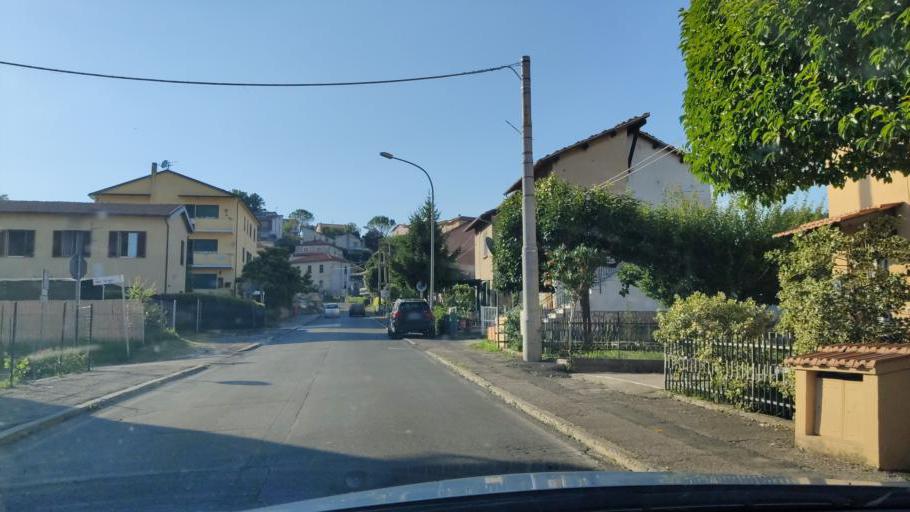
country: IT
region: Umbria
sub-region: Provincia di Terni
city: Narni Scalo
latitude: 42.5388
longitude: 12.5192
